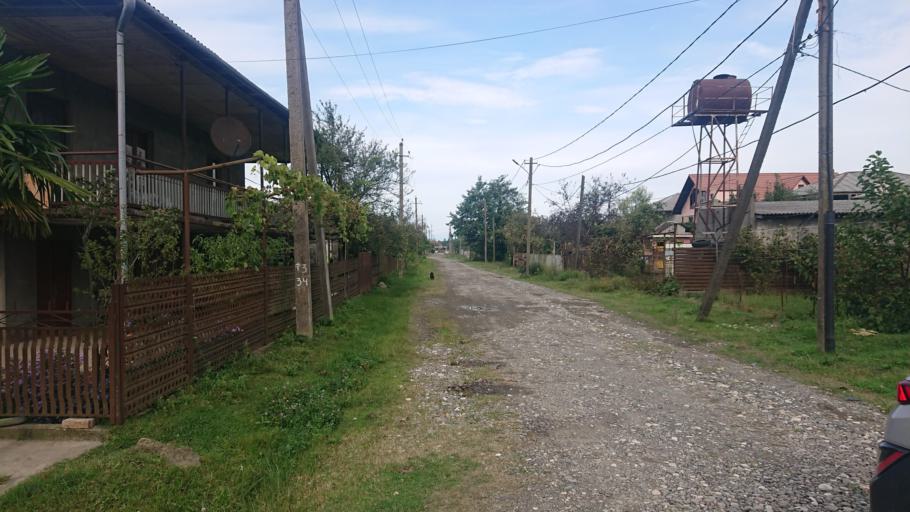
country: GE
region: Samegrelo and Zemo Svaneti
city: P'ot'i
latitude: 42.1283
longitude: 41.6889
